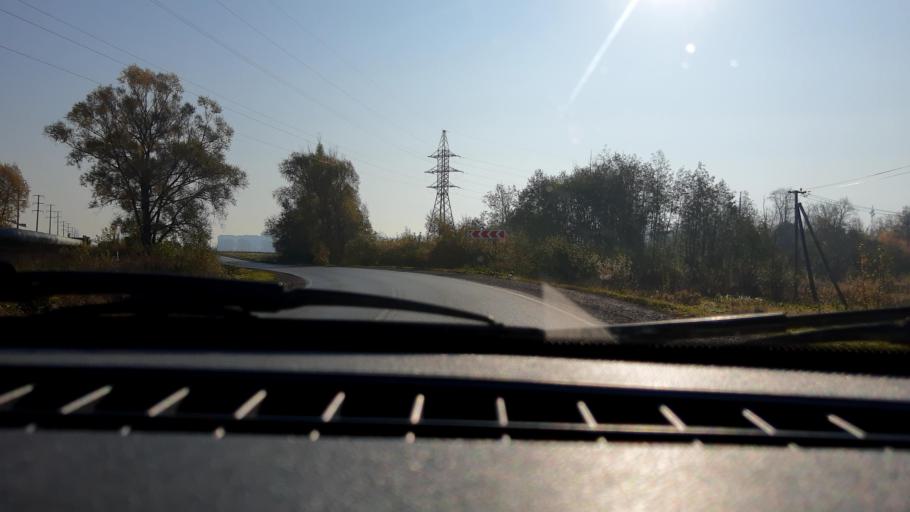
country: RU
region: Bashkortostan
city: Mikhaylovka
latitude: 54.8001
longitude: 55.8370
